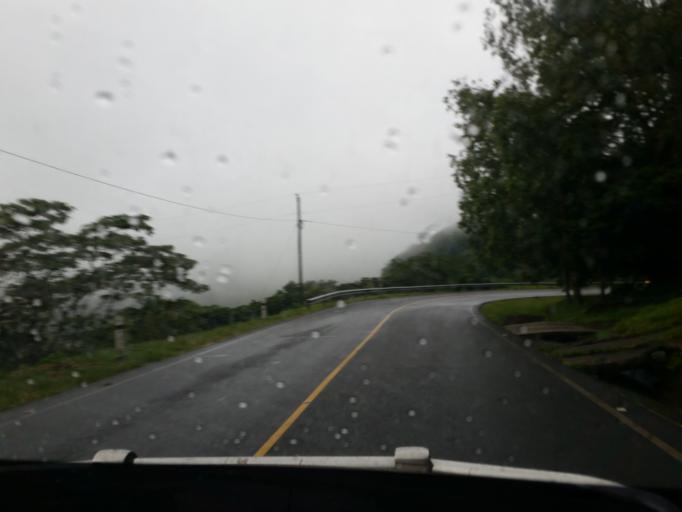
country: NI
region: Matagalpa
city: Matagalpa
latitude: 12.9792
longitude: -85.9219
